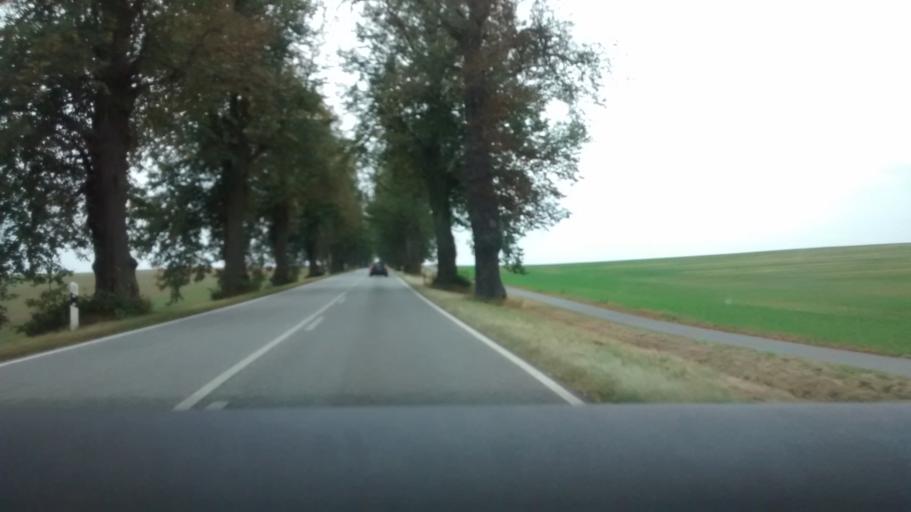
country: DE
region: Mecklenburg-Vorpommern
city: Mecklenburg
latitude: 53.8368
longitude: 11.4572
